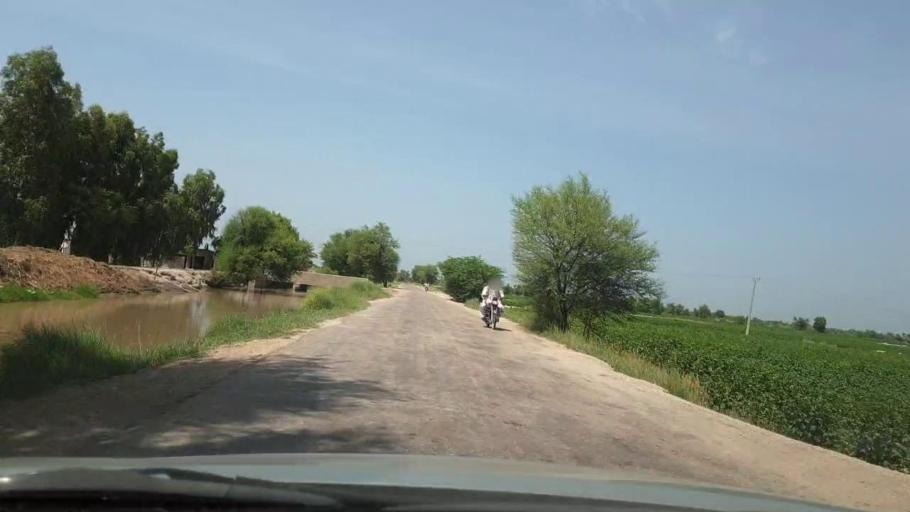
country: PK
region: Sindh
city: Pano Aqil
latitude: 27.6747
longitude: 69.1091
